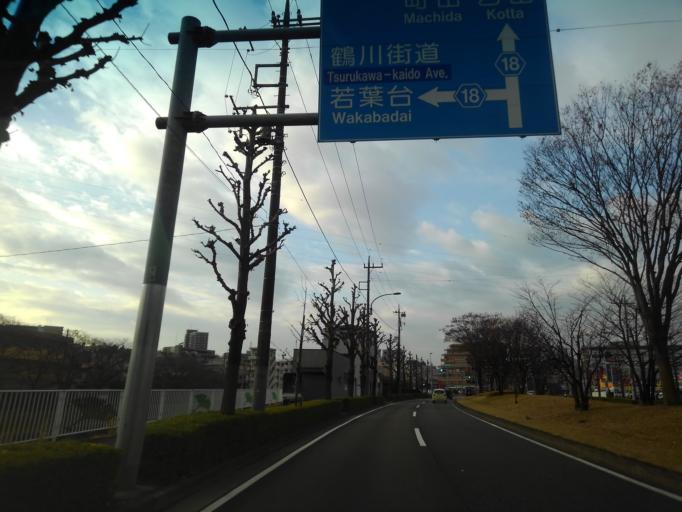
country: JP
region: Tokyo
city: Hino
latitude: 35.6370
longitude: 139.4493
